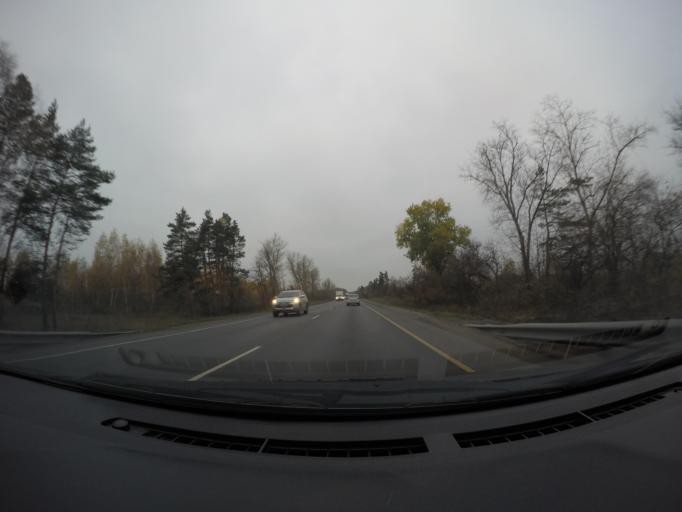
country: RU
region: Moskovskaya
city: Malyshevo
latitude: 55.4588
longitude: 38.3307
